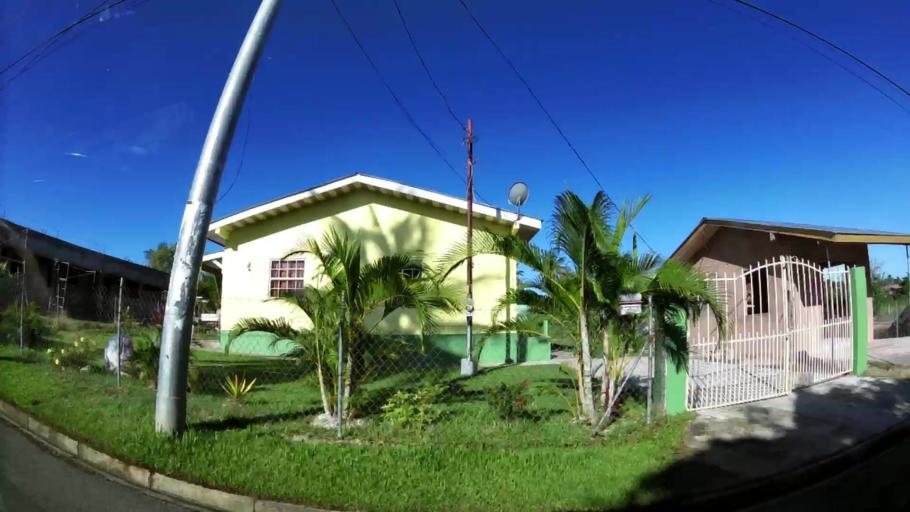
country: TT
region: Tobago
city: Scarborough
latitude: 11.1532
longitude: -60.8209
